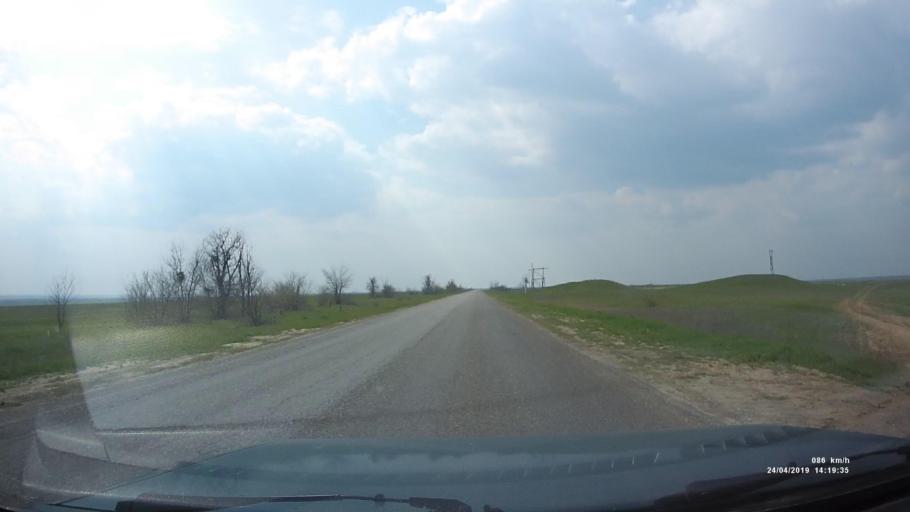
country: RU
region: Kalmykiya
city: Arshan'
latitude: 46.3059
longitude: 44.1730
